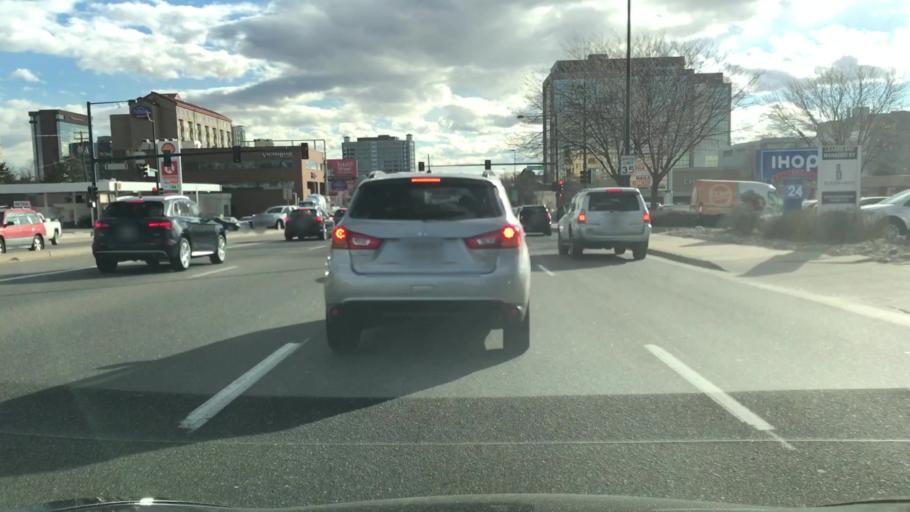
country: US
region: Colorado
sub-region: Arapahoe County
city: Glendale
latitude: 39.6882
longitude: -104.9408
